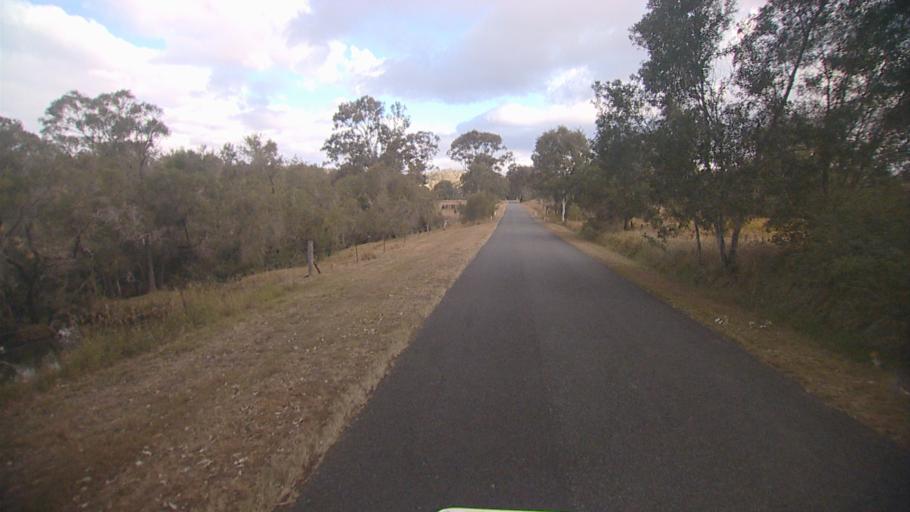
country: AU
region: Queensland
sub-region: Logan
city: Cedar Vale
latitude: -27.8935
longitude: 153.0652
